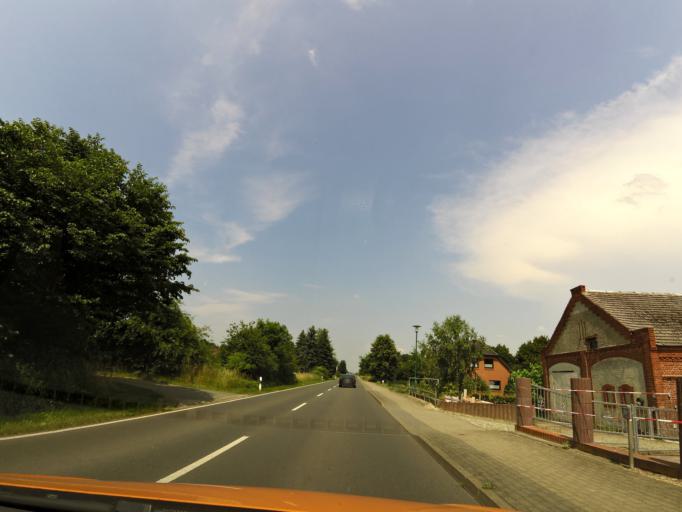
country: DE
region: Brandenburg
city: Pritzwalk
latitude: 53.1939
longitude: 12.1983
